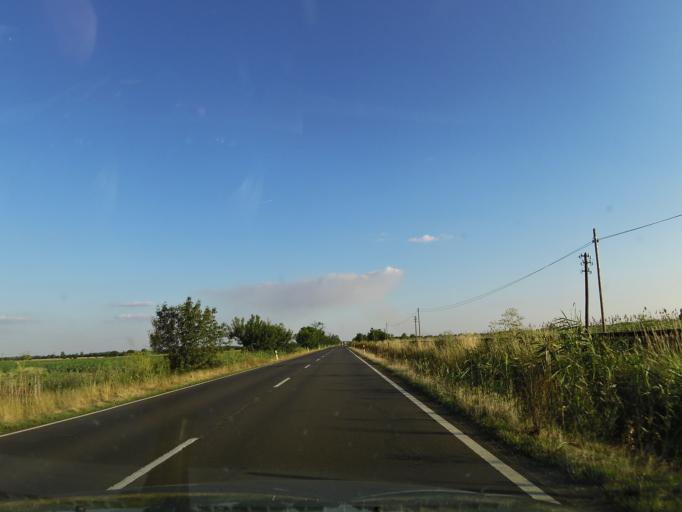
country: HU
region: Jasz-Nagykun-Szolnok
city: Kunszentmarton
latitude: 46.8907
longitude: 20.2690
